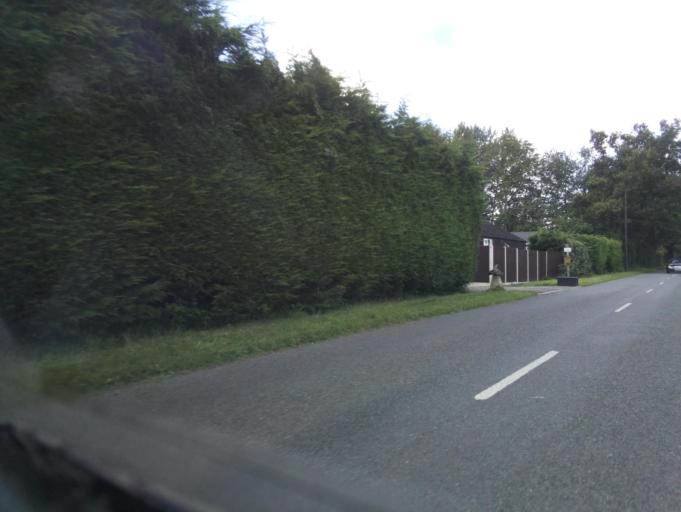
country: GB
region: England
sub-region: Hampshire
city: Overton
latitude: 51.2463
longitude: -1.3334
